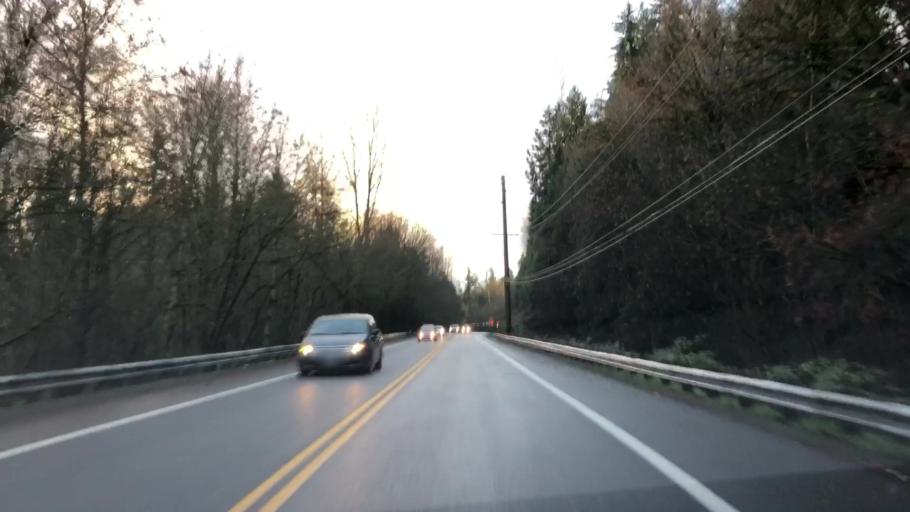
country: US
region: Washington
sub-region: King County
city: Sammamish
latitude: 47.6477
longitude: -122.0560
